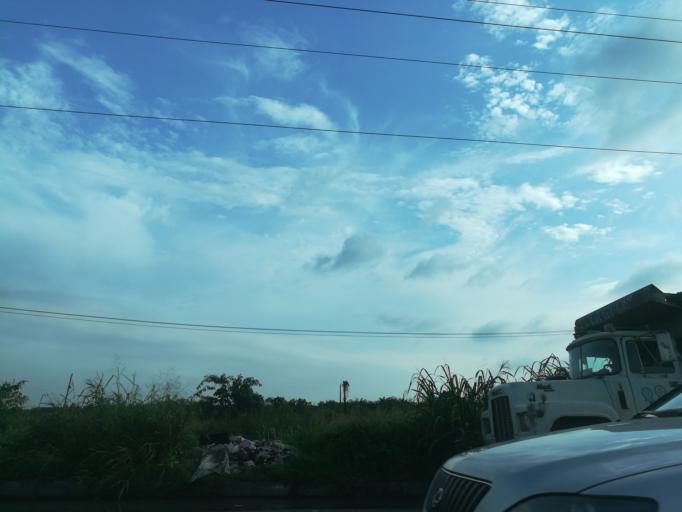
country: NG
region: Lagos
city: Ebute Ikorodu
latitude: 6.6189
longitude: 3.4660
